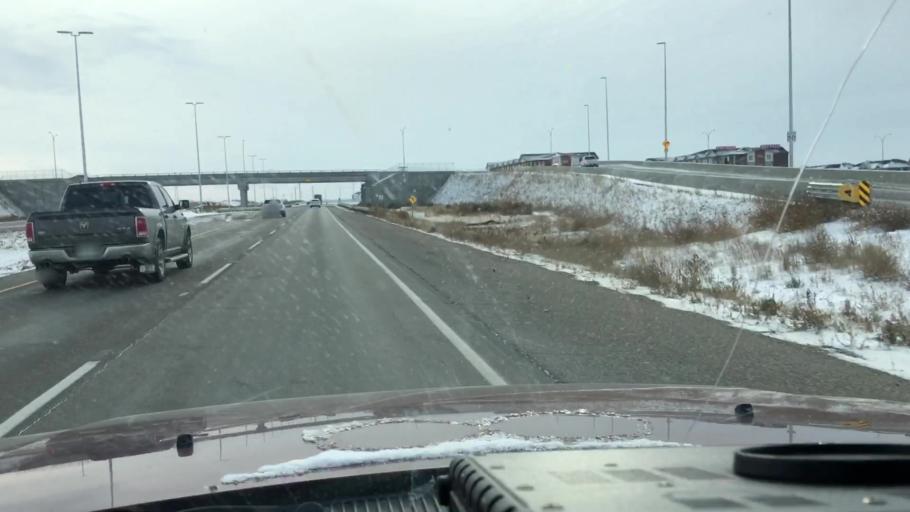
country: CA
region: Saskatchewan
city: Saskatoon
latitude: 52.0803
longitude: -106.6051
